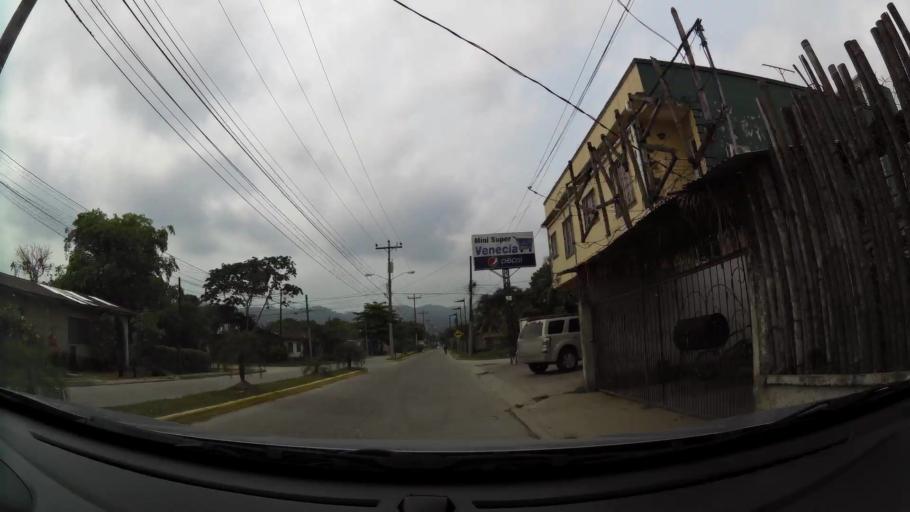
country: HN
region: Atlantida
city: Tela
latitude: 15.7671
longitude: -87.4809
